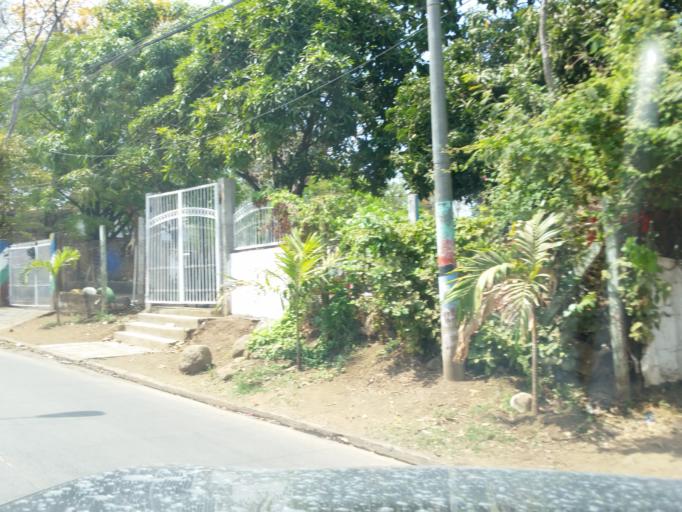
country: NI
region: Masaya
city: Ticuantepe
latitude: 12.0698
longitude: -86.2111
